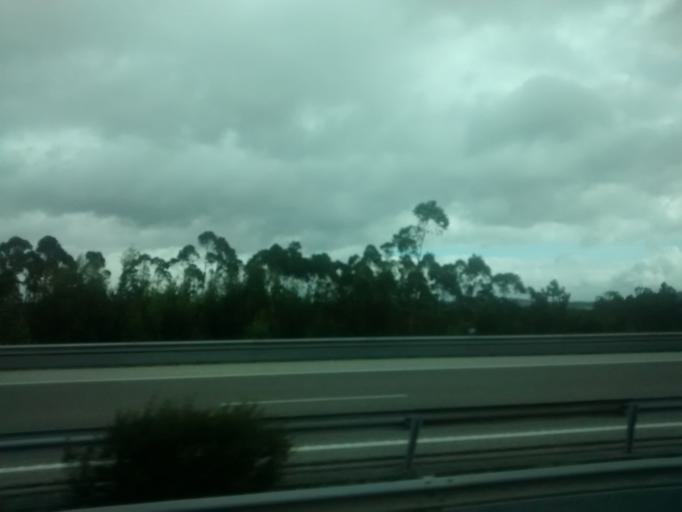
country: PT
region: Santarem
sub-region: Ourem
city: Fatima
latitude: 39.5778
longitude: -8.6548
